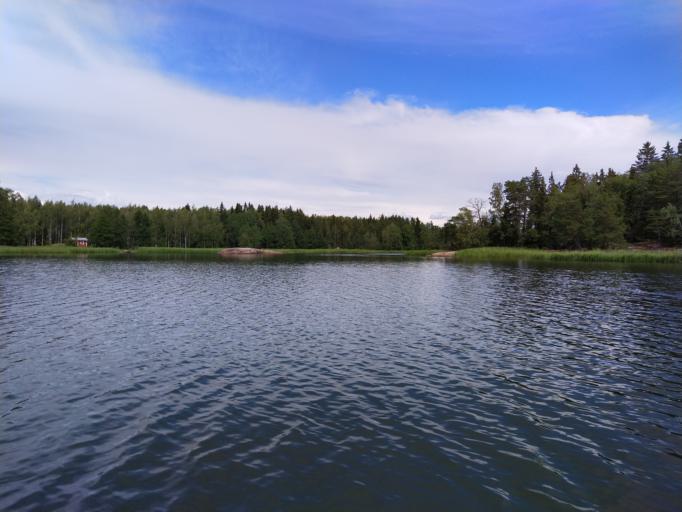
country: FI
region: Uusimaa
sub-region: Raaseporin
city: Karis
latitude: 59.9706
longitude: 23.7022
